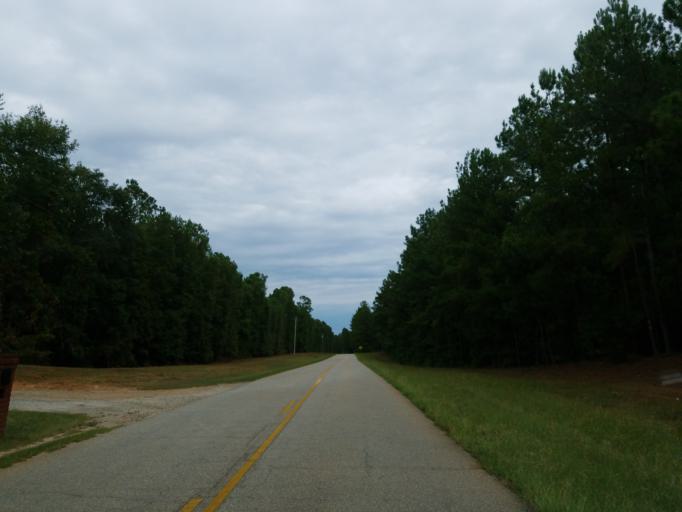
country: US
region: Georgia
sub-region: Monroe County
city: Forsyth
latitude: 32.9750
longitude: -83.9877
